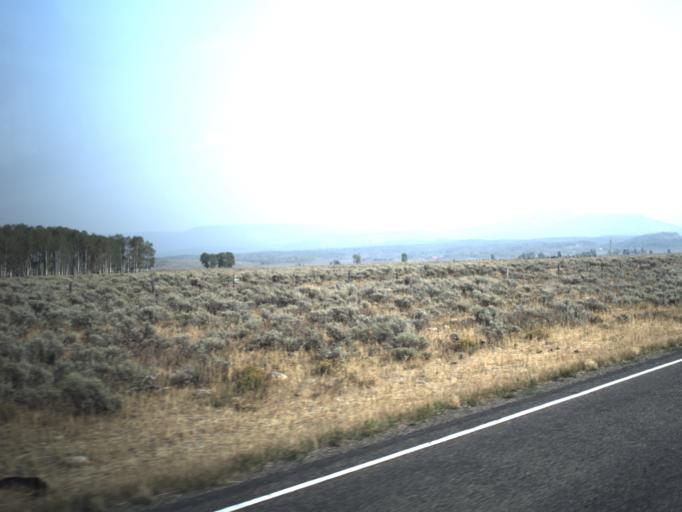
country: US
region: Wyoming
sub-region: Uinta County
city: Evanston
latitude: 40.9634
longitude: -110.8459
